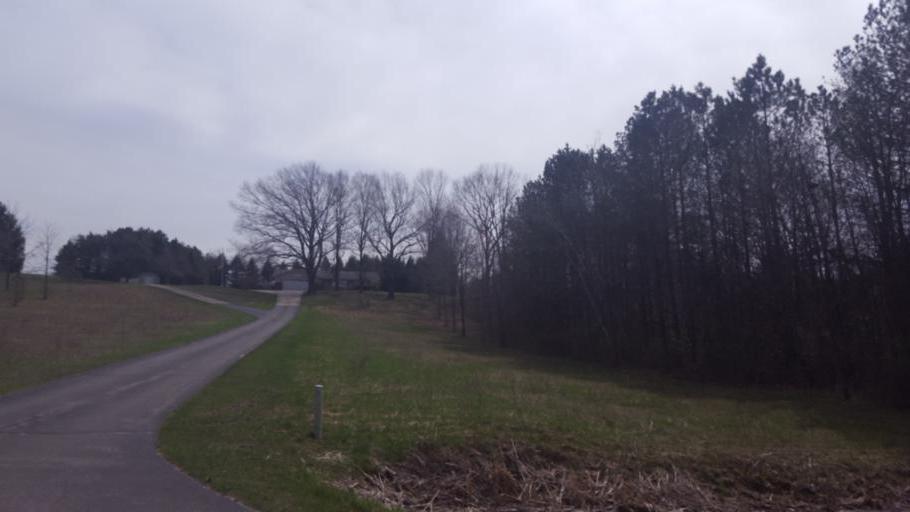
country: US
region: Michigan
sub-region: Gladwin County
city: Gladwin
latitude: 43.9878
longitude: -84.5359
